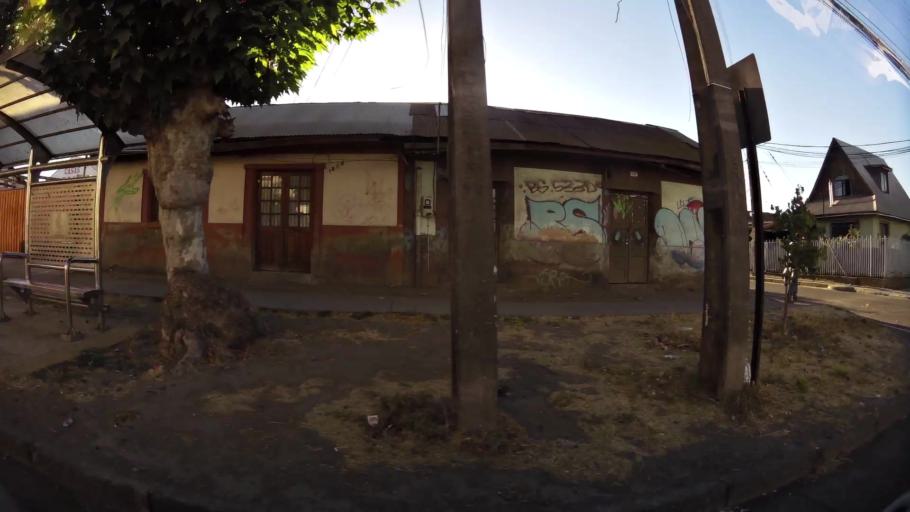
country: CL
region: Maule
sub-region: Provincia de Curico
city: Curico
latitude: -34.9786
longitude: -71.2481
